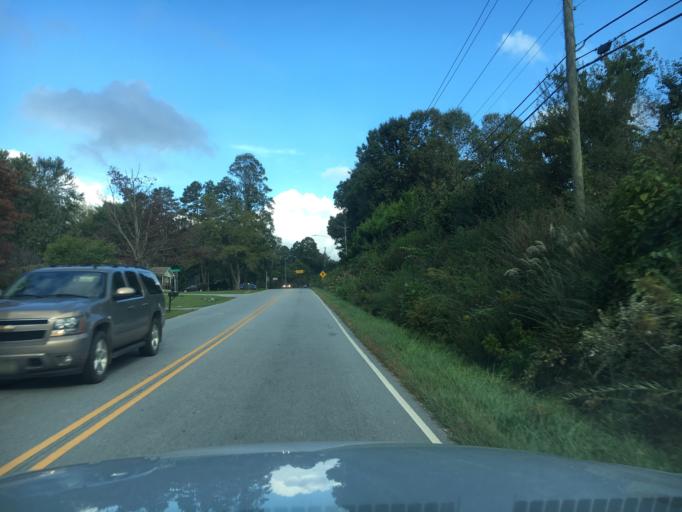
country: US
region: North Carolina
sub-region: Henderson County
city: Fletcher
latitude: 35.4345
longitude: -82.5149
